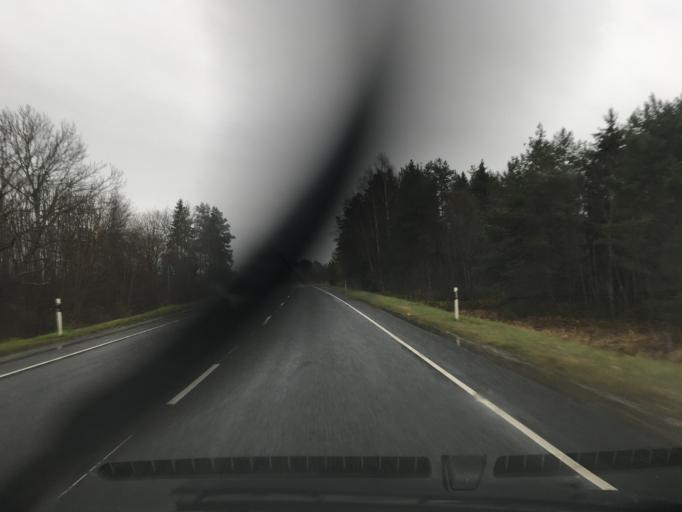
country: EE
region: Harju
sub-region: Nissi vald
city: Turba
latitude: 58.9329
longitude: 24.0981
